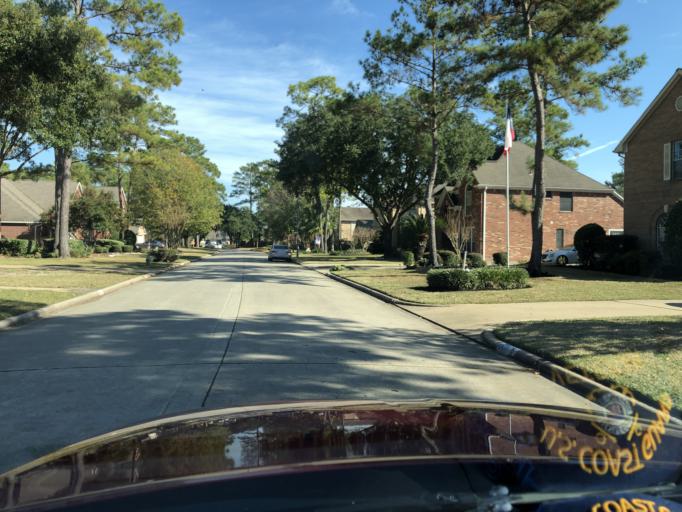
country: US
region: Texas
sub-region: Harris County
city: Tomball
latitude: 30.0197
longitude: -95.5528
